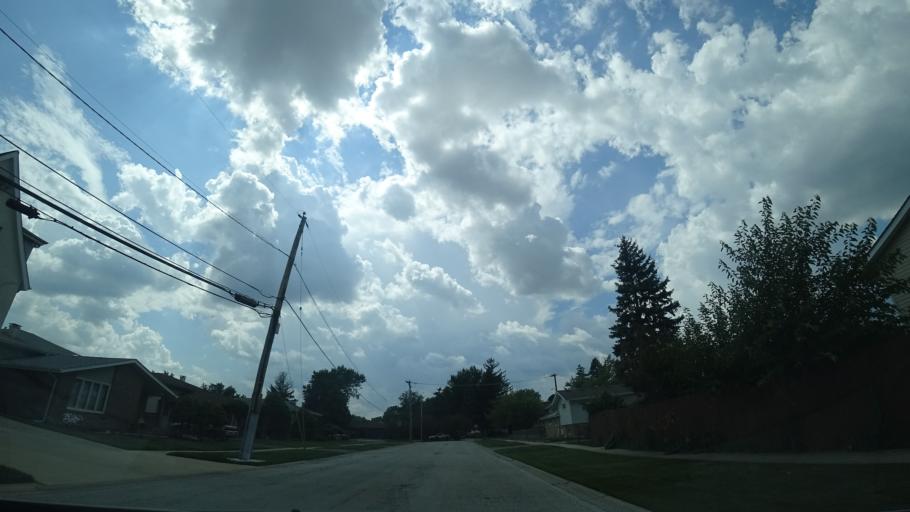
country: US
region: Illinois
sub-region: Cook County
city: Alsip
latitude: 41.6746
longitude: -87.7236
